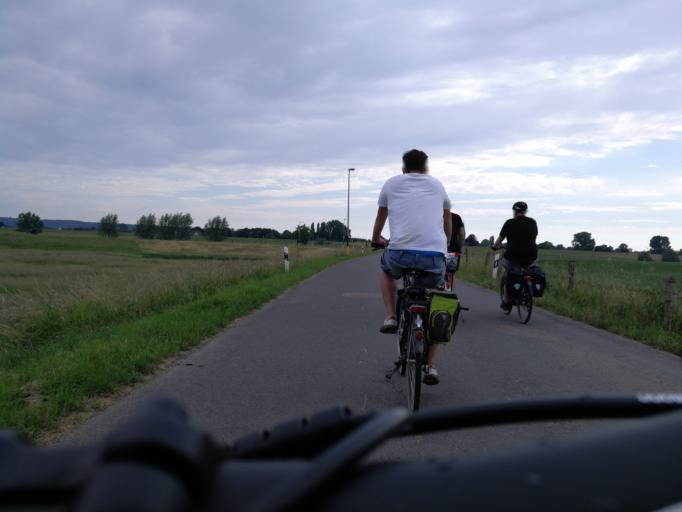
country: DE
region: North Rhine-Westphalia
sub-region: Regierungsbezirk Dusseldorf
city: Kleve
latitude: 51.8345
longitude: 6.1115
